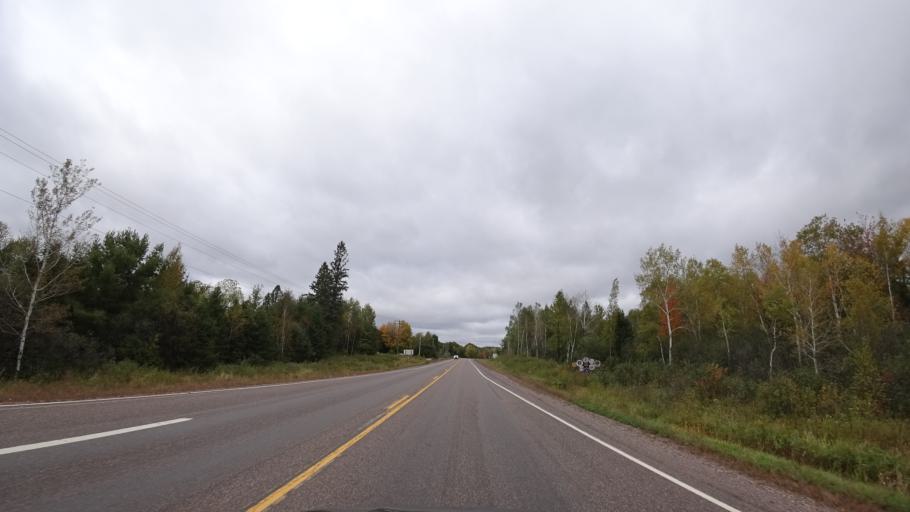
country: US
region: Wisconsin
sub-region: Rusk County
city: Ladysmith
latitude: 45.4443
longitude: -91.1111
